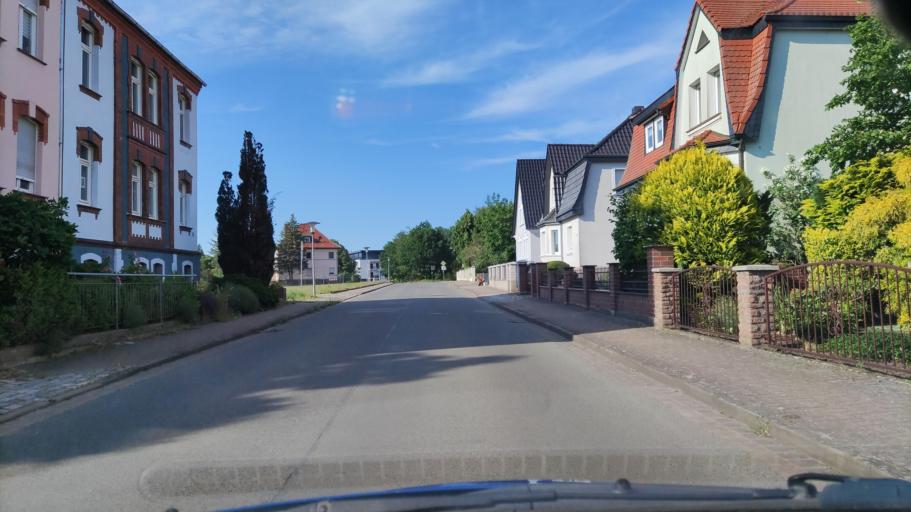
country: DE
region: Saxony-Anhalt
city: Gardelegen
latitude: 52.5297
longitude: 11.3882
